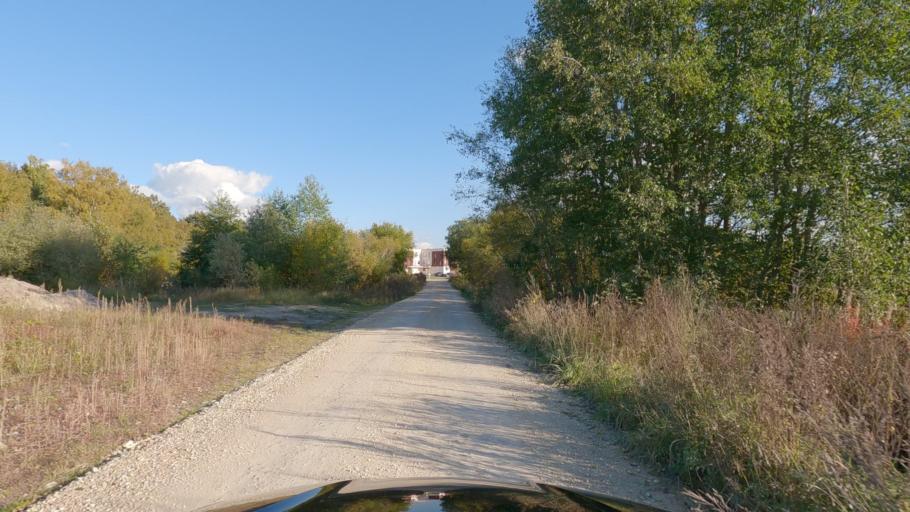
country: EE
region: Harju
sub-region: Saue vald
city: Laagri
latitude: 59.3484
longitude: 24.6453
